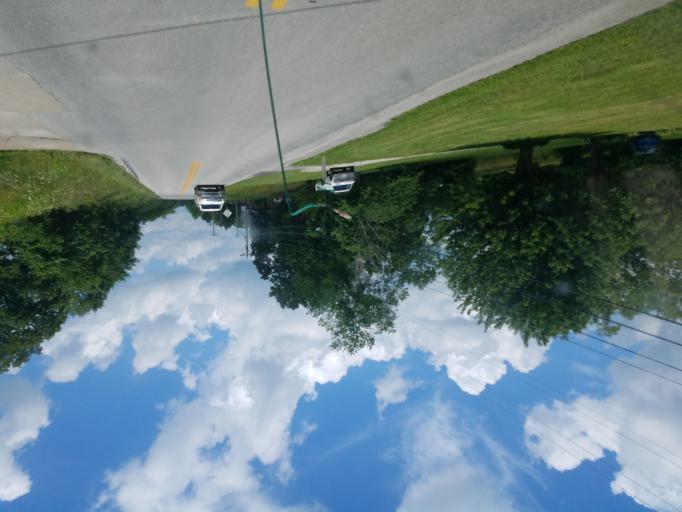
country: US
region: Kentucky
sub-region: Grayson County
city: Leitchfield
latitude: 37.5010
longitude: -86.3108
